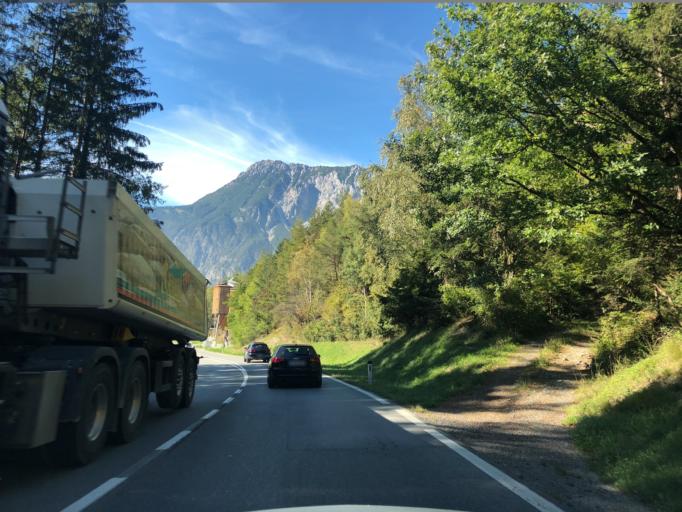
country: AT
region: Tyrol
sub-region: Politischer Bezirk Imst
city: Sautens
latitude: 47.2188
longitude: 10.8656
